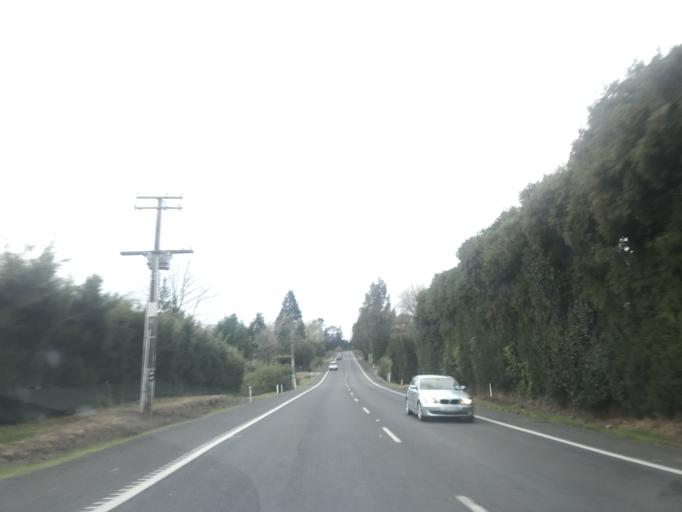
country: NZ
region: Bay of Plenty
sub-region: Western Bay of Plenty District
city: Katikati
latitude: -37.4873
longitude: 175.9294
